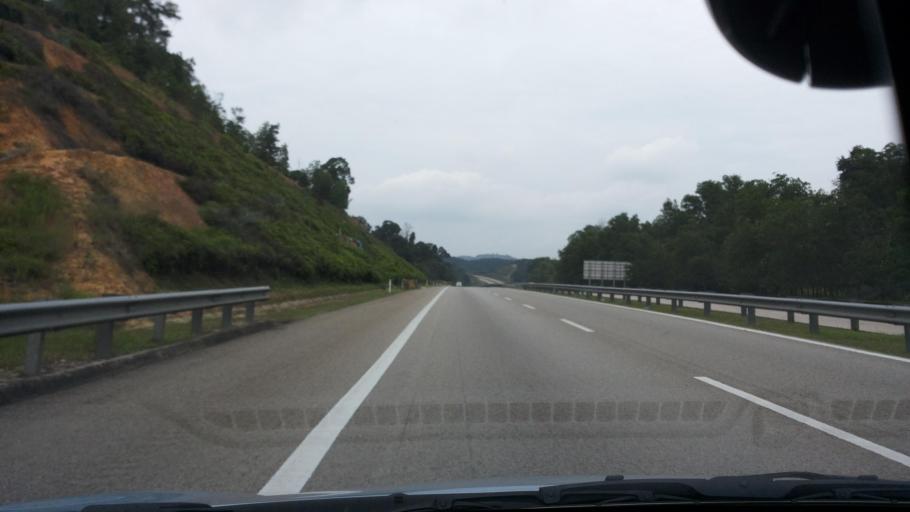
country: MY
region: Pahang
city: Kuantan
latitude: 3.7738
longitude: 103.1485
